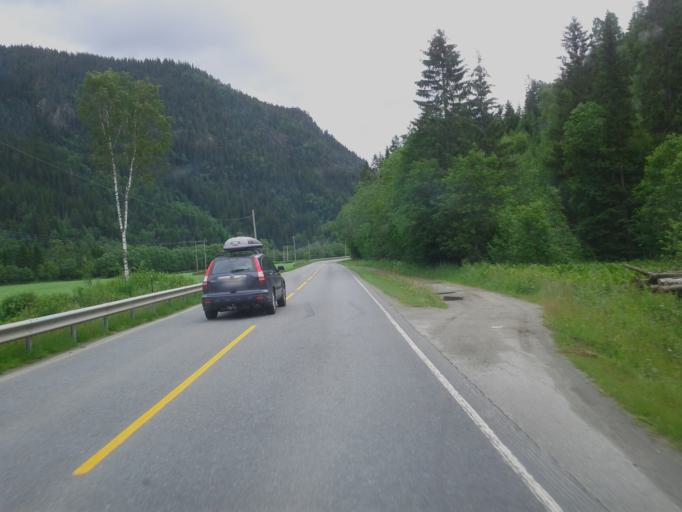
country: NO
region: Sor-Trondelag
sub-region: Midtre Gauldal
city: Storen
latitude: 62.9908
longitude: 10.5294
